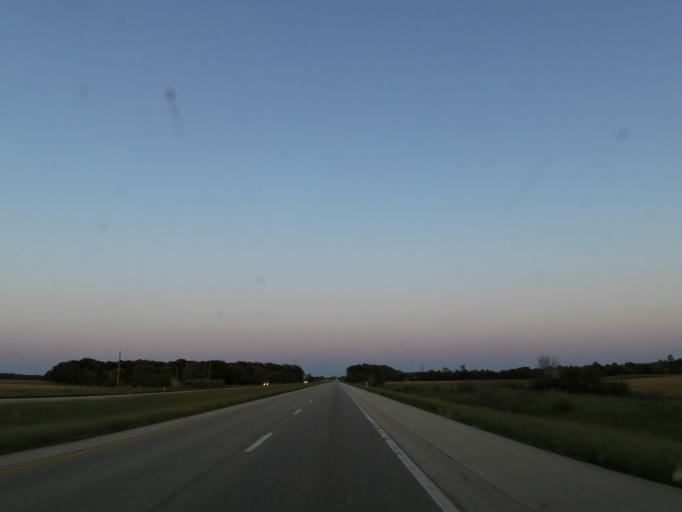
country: US
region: Indiana
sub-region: Montgomery County
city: Crawfordsville
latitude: 40.0184
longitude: -86.7729
